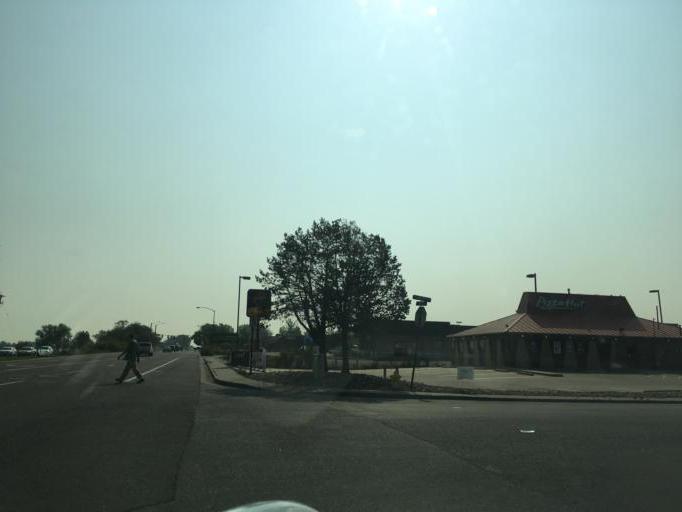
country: US
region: Colorado
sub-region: Adams County
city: Brighton
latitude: 39.9867
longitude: -104.7951
